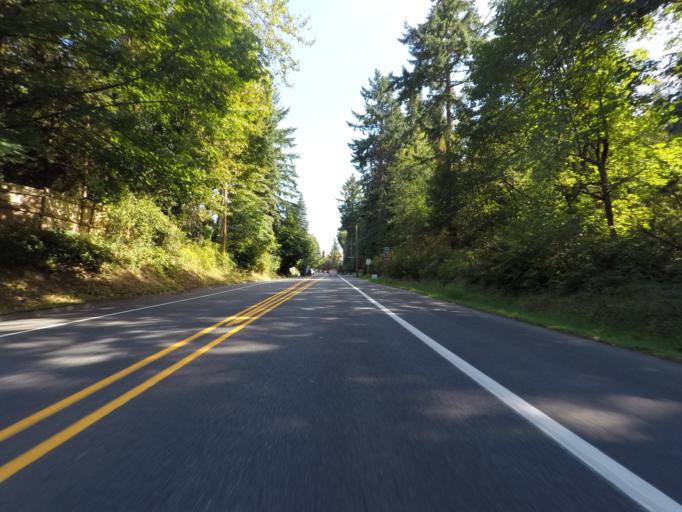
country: US
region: Washington
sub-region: King County
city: Inglewood-Finn Hill
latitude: 47.7342
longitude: -122.2470
